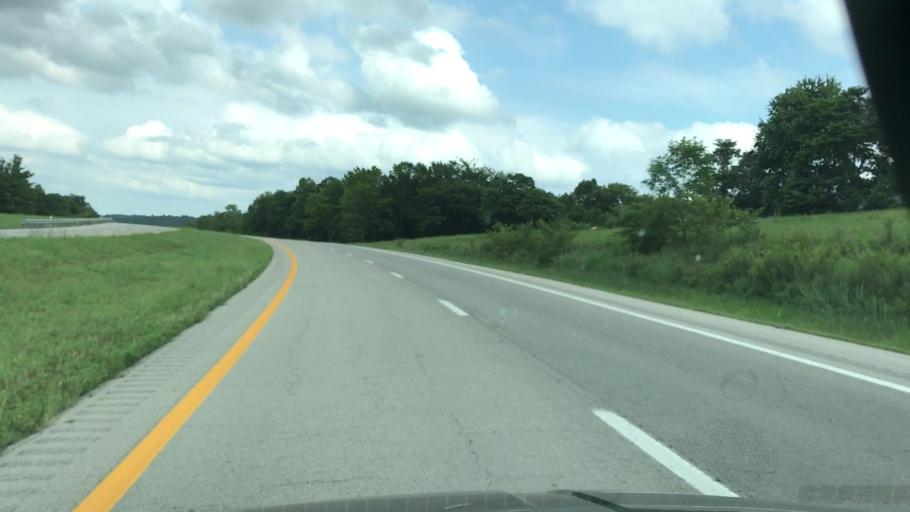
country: US
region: Kentucky
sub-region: Caldwell County
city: Princeton
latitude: 37.1403
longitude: -87.8155
